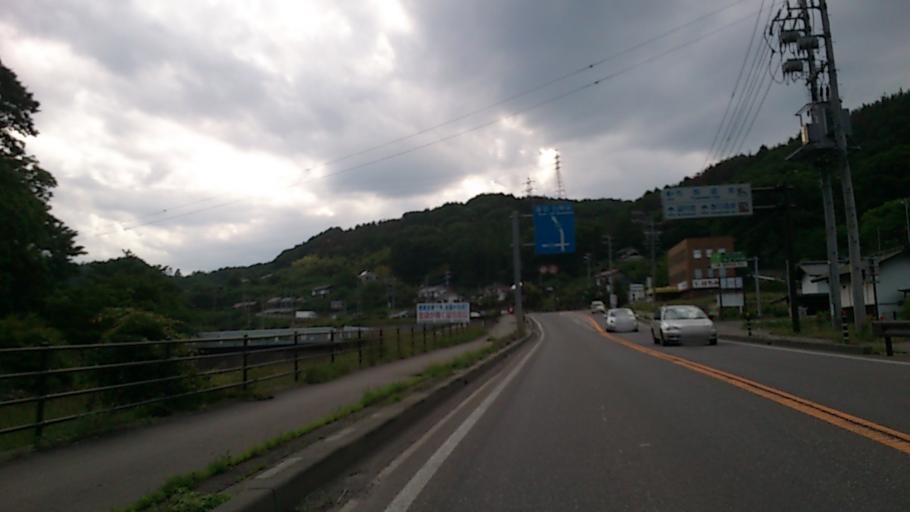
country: JP
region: Nagano
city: Komoro
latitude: 36.2688
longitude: 138.3796
